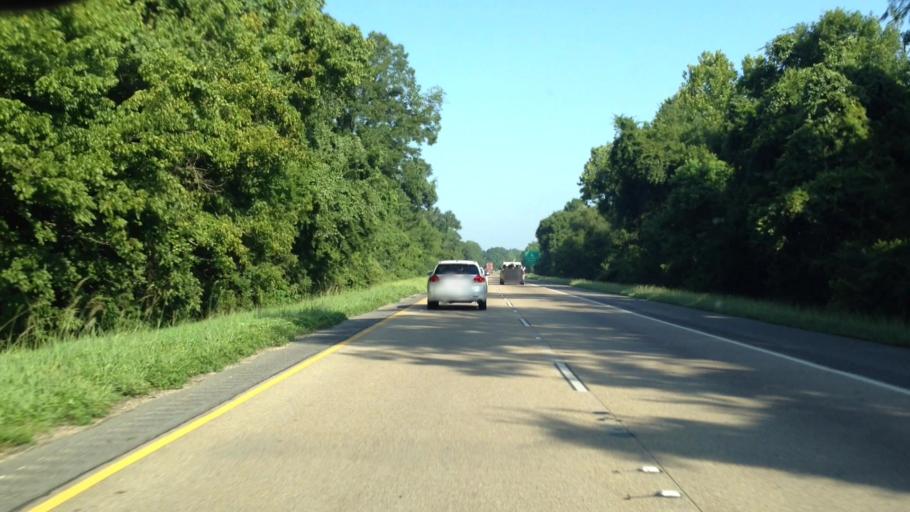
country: US
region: Louisiana
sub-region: Ascension Parish
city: Gonzales
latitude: 30.1966
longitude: -90.9283
